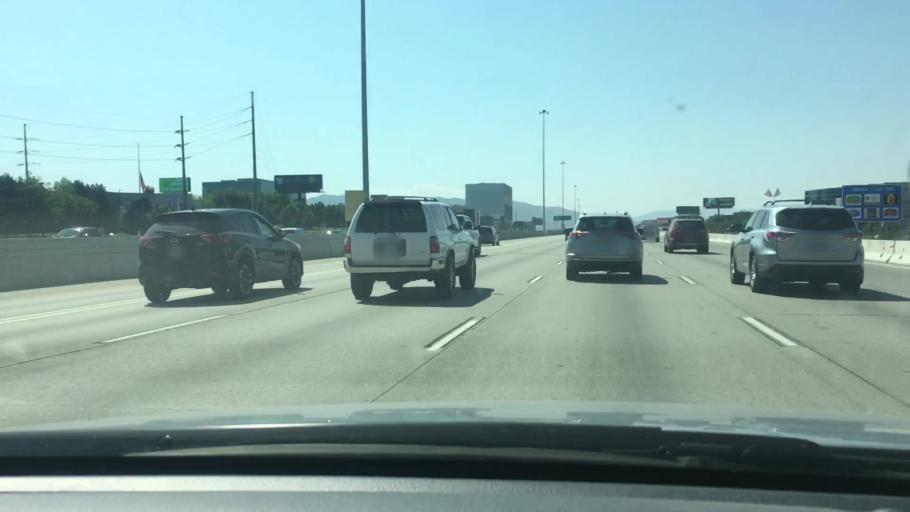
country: US
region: Utah
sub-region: Salt Lake County
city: Sandy City
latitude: 40.5800
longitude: -111.9011
